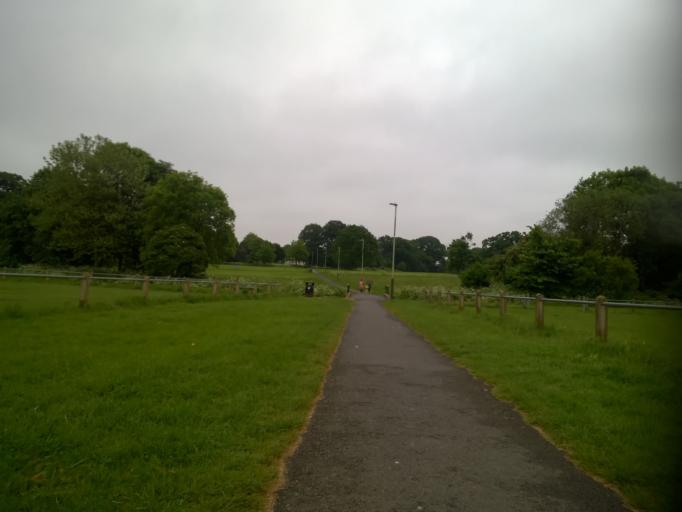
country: GB
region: England
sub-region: Leicestershire
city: Glenfield
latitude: 52.6277
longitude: -1.1816
